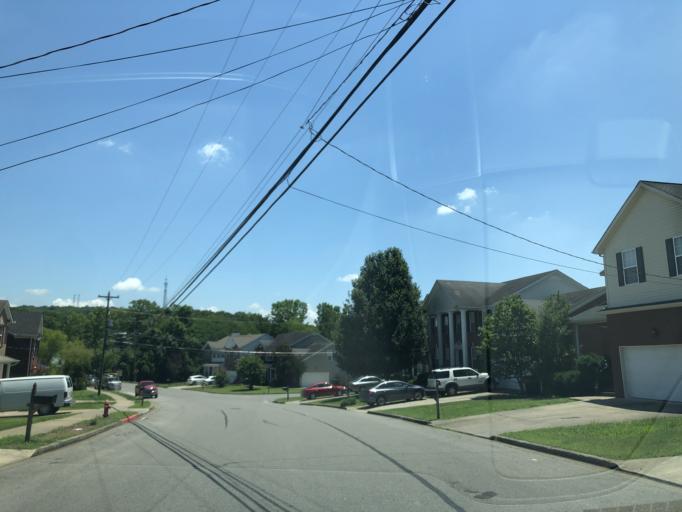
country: US
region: Tennessee
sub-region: Rutherford County
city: La Vergne
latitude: 36.0200
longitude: -86.6506
